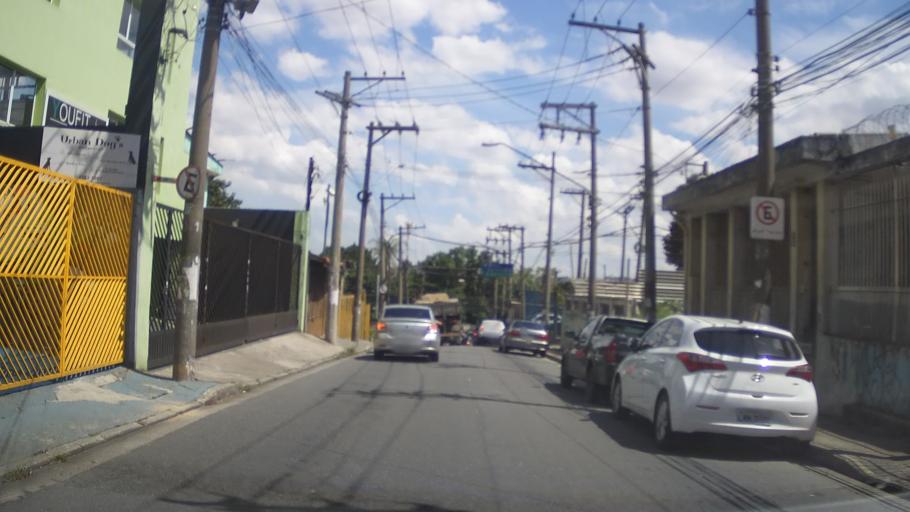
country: BR
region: Sao Paulo
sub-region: Guarulhos
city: Guarulhos
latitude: -23.4674
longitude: -46.5160
